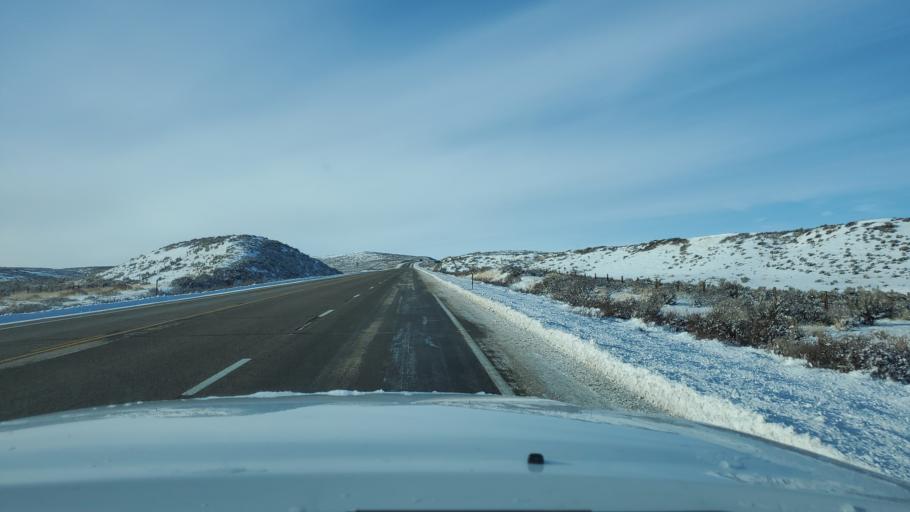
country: US
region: Colorado
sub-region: Rio Blanco County
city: Meeker
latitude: 40.5142
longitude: -108.1021
